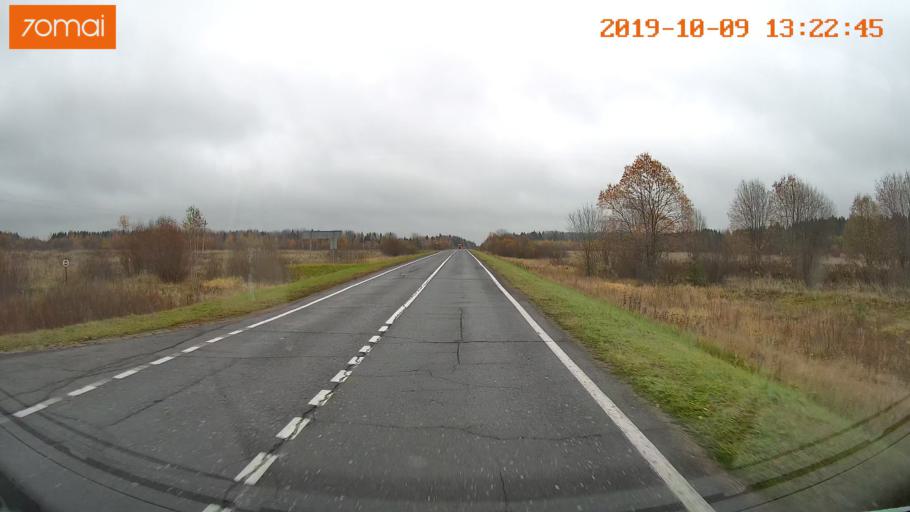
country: RU
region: Jaroslavl
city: Lyubim
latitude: 58.3386
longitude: 40.8723
